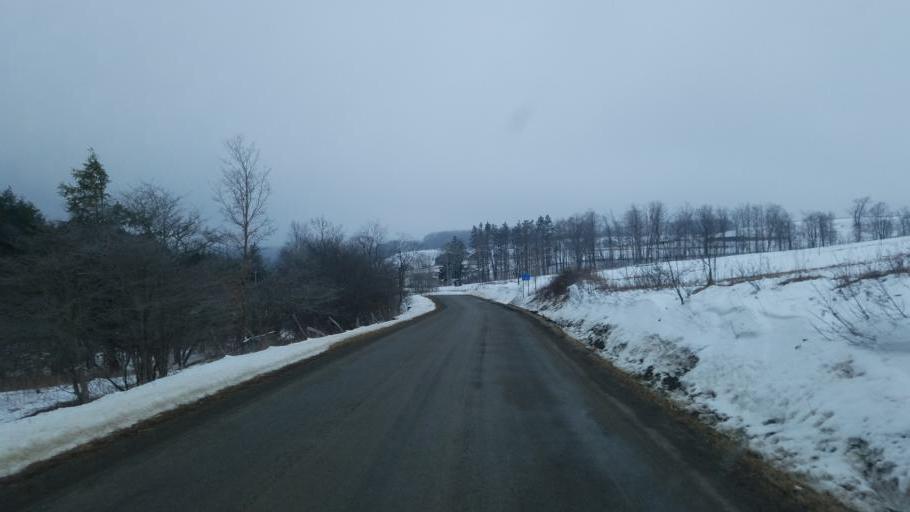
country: US
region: New York
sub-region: Allegany County
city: Andover
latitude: 41.9577
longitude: -77.7699
